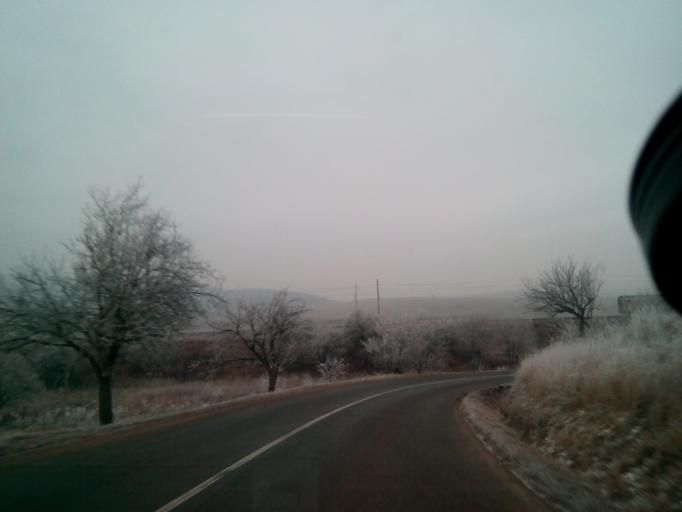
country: SK
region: Presovsky
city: Lubica
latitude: 48.9875
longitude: 20.4215
